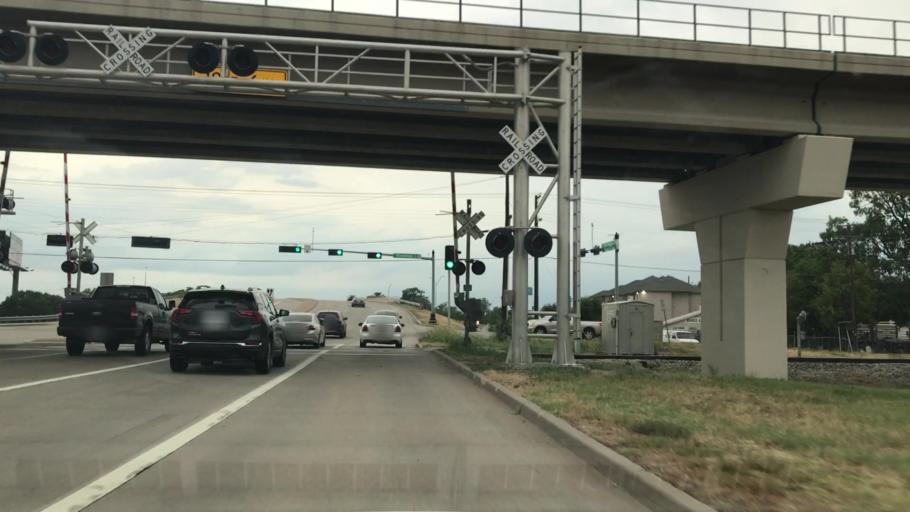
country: US
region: Texas
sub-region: Dallas County
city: Carrollton
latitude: 32.9649
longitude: -96.9150
